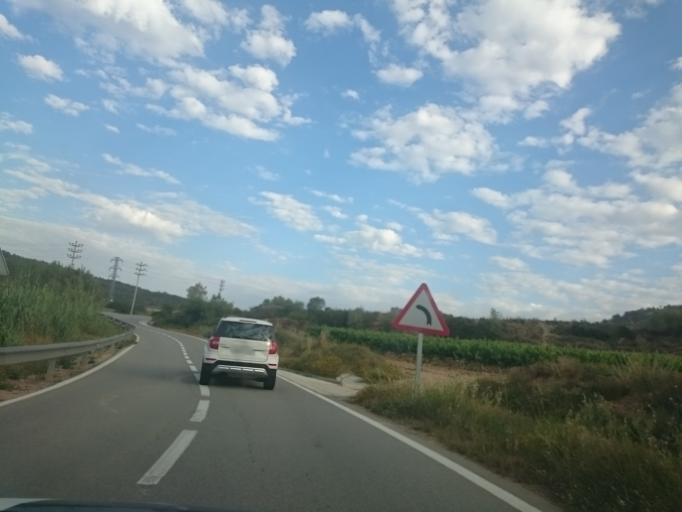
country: ES
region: Catalonia
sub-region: Provincia de Barcelona
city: Castellet
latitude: 41.2516
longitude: 1.6576
